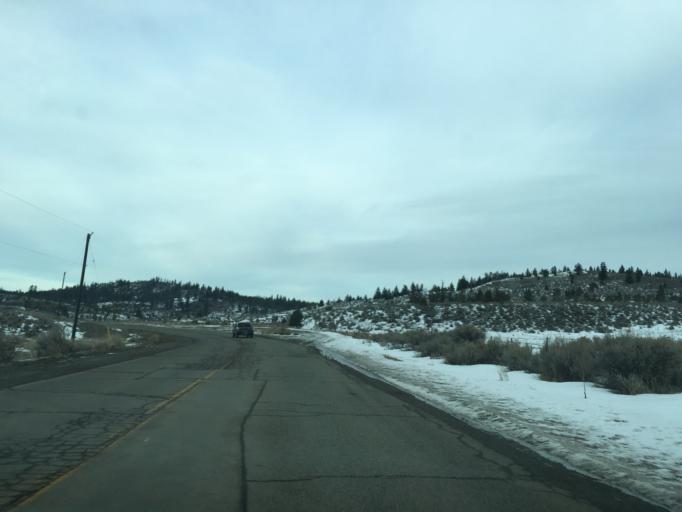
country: CA
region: British Columbia
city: Kamloops
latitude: 50.6270
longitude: -120.4420
